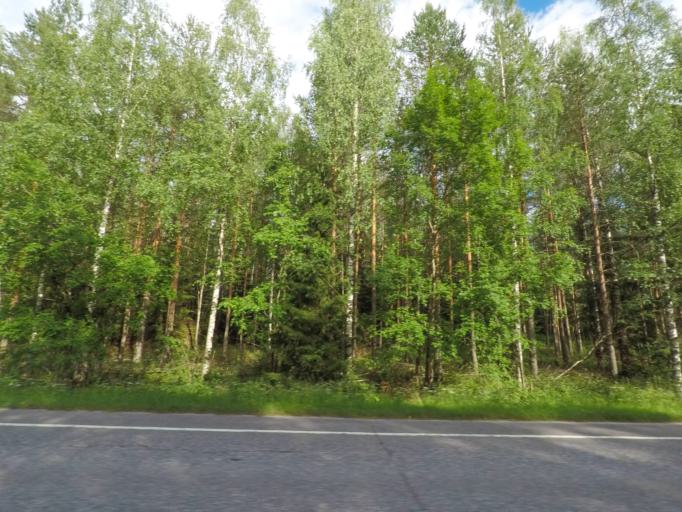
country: FI
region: Paijanne Tavastia
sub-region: Lahti
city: Hollola
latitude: 60.8165
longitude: 25.4831
